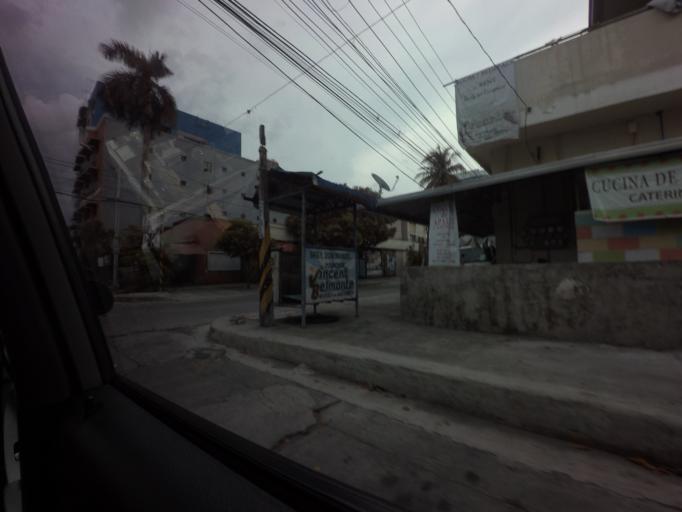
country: PH
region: Metro Manila
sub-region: City of Manila
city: Manila
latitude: 14.6172
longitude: 121.0053
